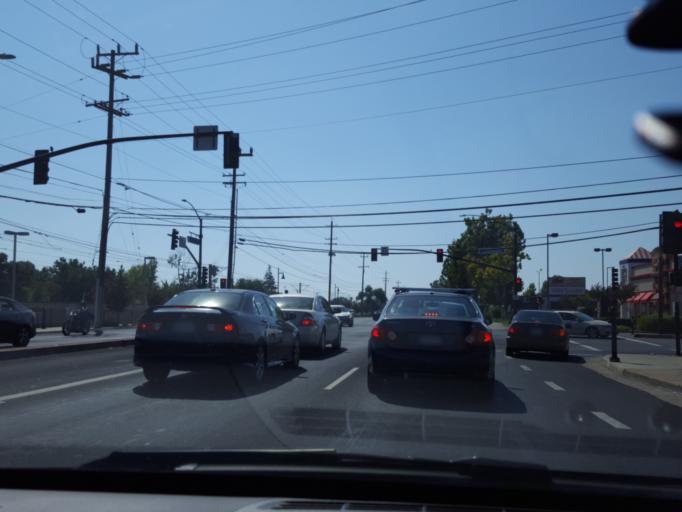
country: US
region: California
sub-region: Sacramento County
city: Rancho Cordova
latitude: 38.5894
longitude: -121.3025
